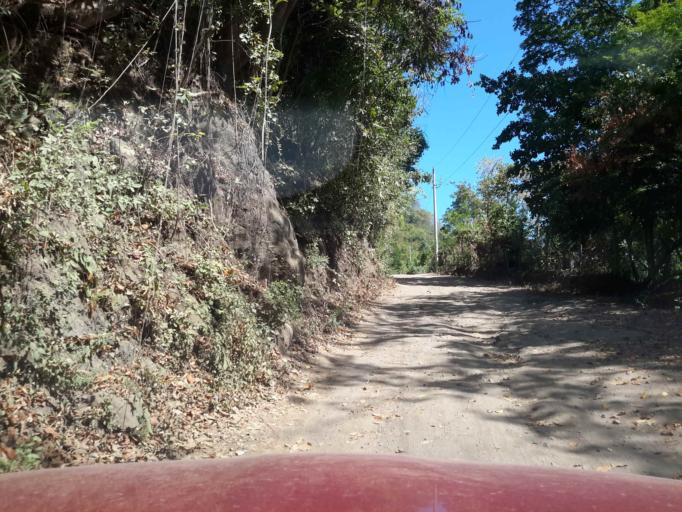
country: NI
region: Masaya
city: Catarina
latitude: 11.9423
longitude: -86.0460
